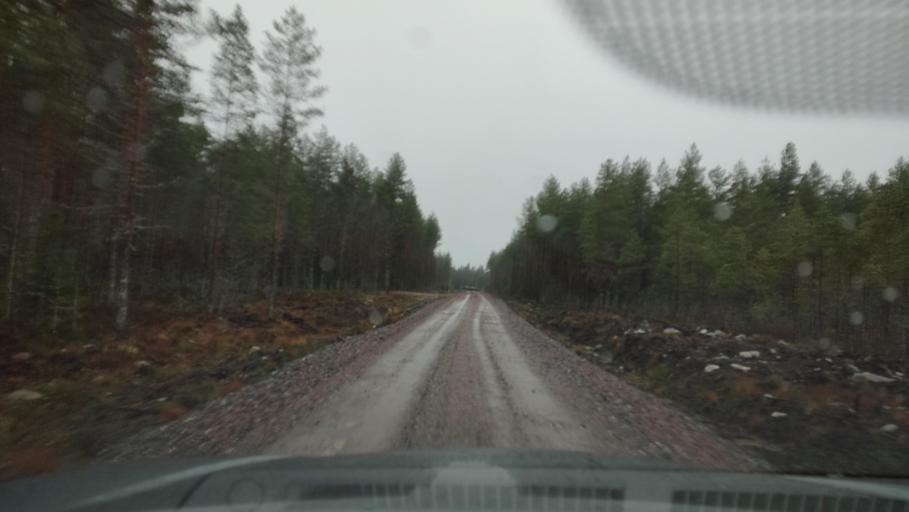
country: FI
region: Southern Ostrobothnia
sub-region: Suupohja
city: Karijoki
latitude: 62.1749
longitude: 21.7088
